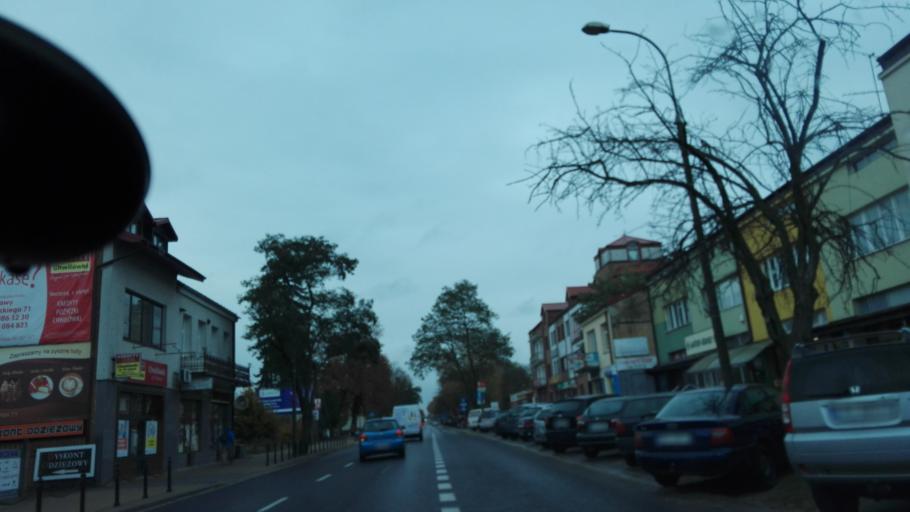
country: PL
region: Lublin Voivodeship
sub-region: Powiat pulawski
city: Pulawy
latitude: 51.4171
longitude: 21.9624
